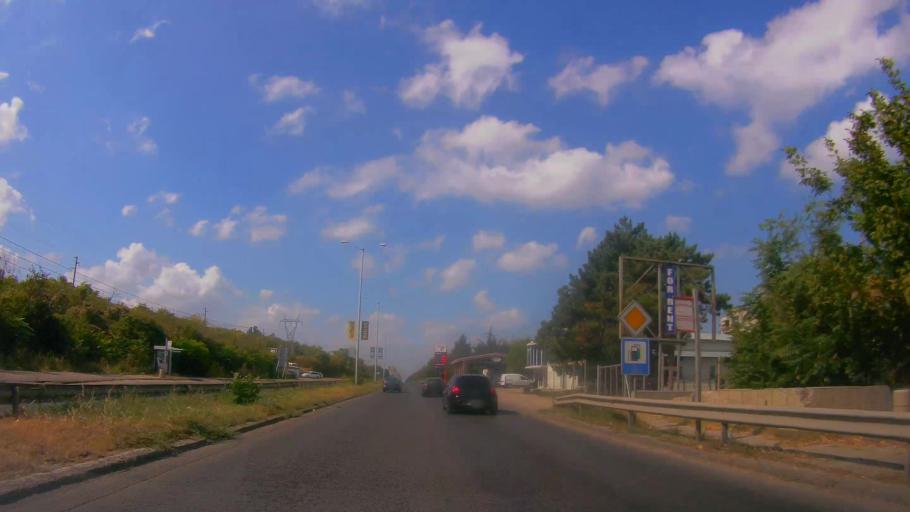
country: BG
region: Ruse
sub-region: Obshtina Ruse
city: Ruse
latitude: 43.8523
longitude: 26.0058
